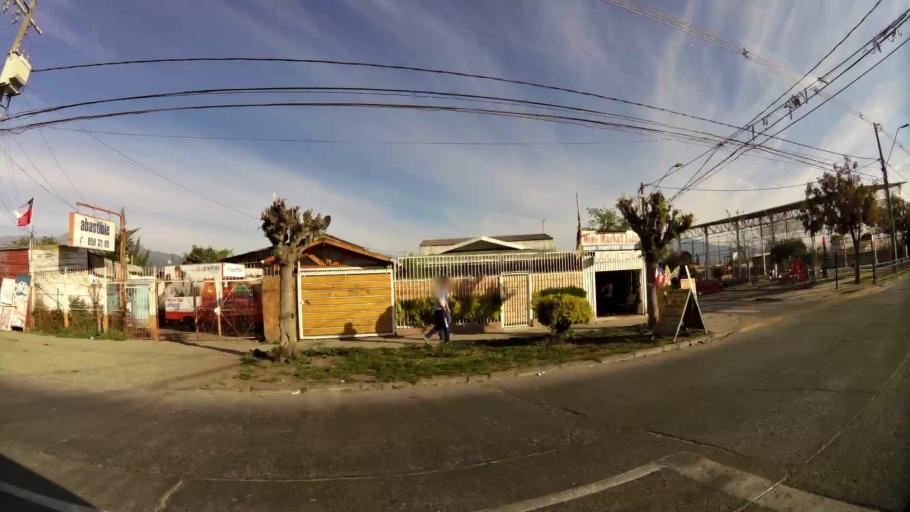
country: CL
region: Santiago Metropolitan
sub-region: Provincia de Cordillera
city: Puente Alto
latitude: -33.6195
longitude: -70.5773
